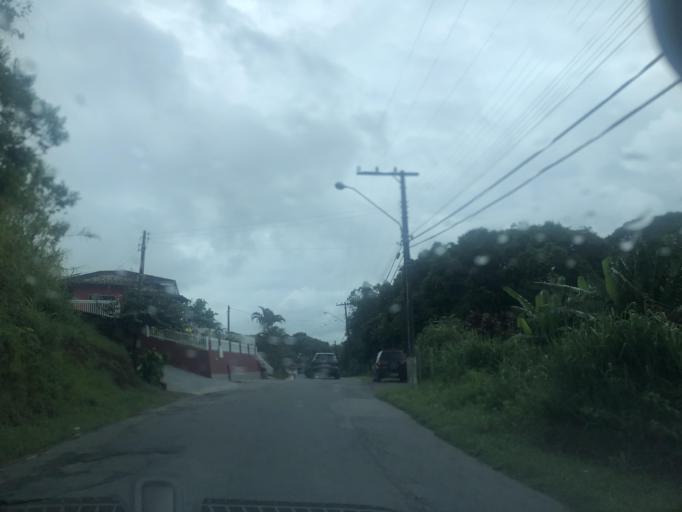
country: BR
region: Santa Catarina
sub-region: Sao Francisco Do Sul
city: Sao Francisco do Sul
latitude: -26.2320
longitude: -48.6125
